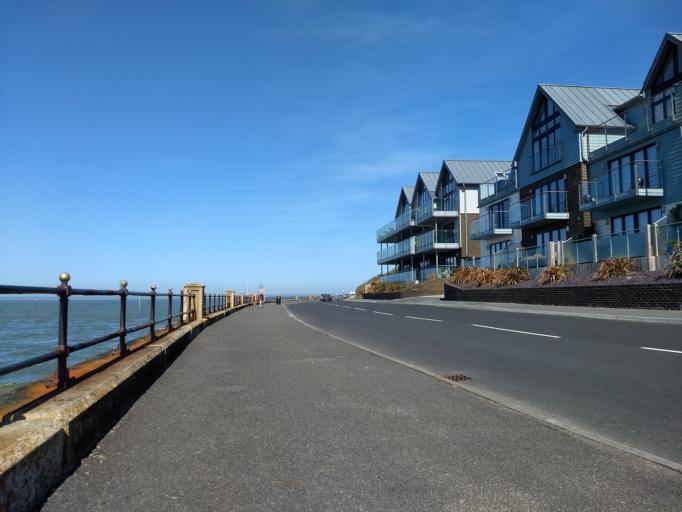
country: GB
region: England
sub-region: Isle of Wight
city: Gurnard
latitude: 50.7636
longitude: -1.3229
